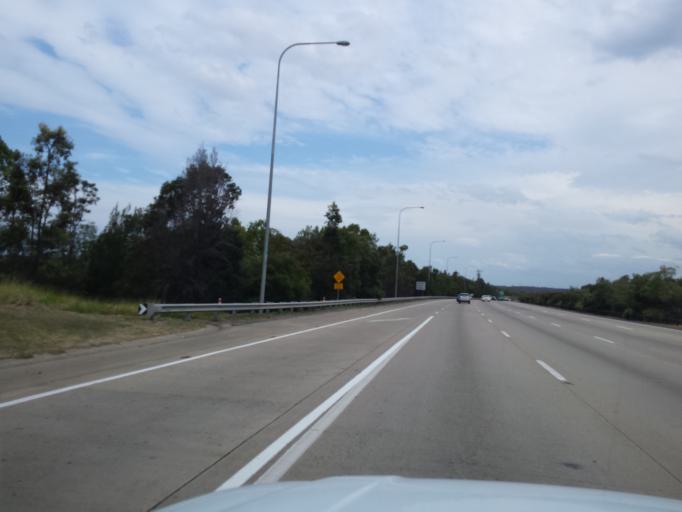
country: AU
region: Queensland
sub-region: Gold Coast
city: Oxenford
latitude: -27.9309
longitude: 153.3335
